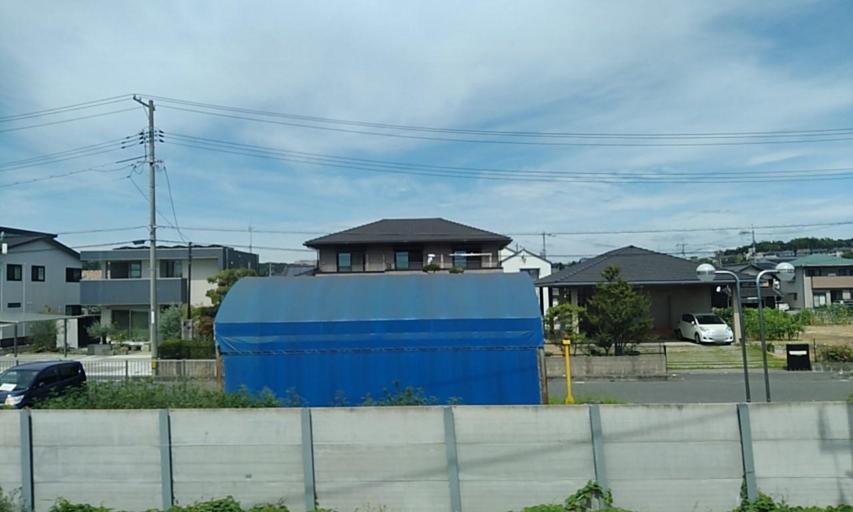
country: JP
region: Okayama
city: Kurashiki
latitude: 34.6033
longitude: 133.8351
